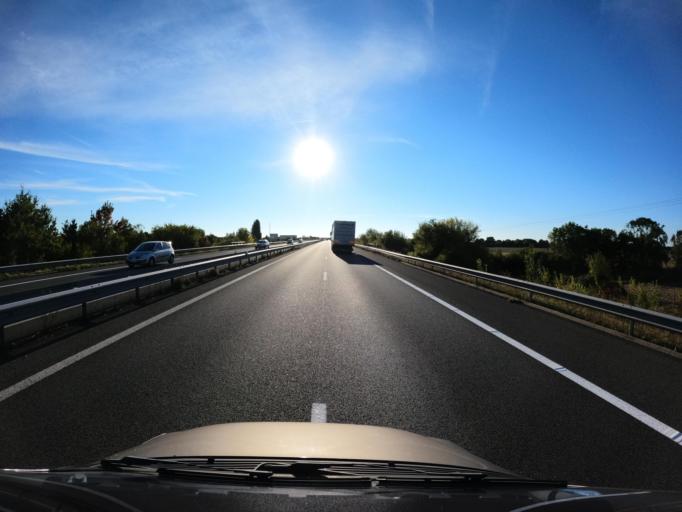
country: FR
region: Pays de la Loire
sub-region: Departement de Maine-et-Loire
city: Chemille-Melay
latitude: 47.2439
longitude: -0.7177
